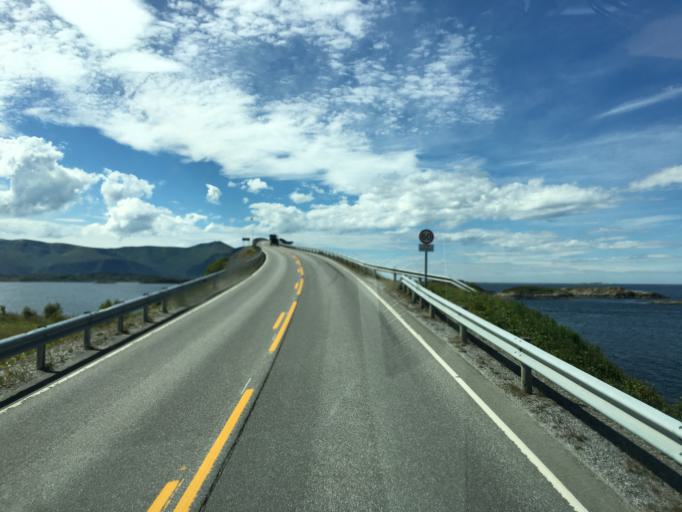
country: NO
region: More og Romsdal
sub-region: Eide
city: Eide
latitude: 63.0178
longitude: 7.3598
